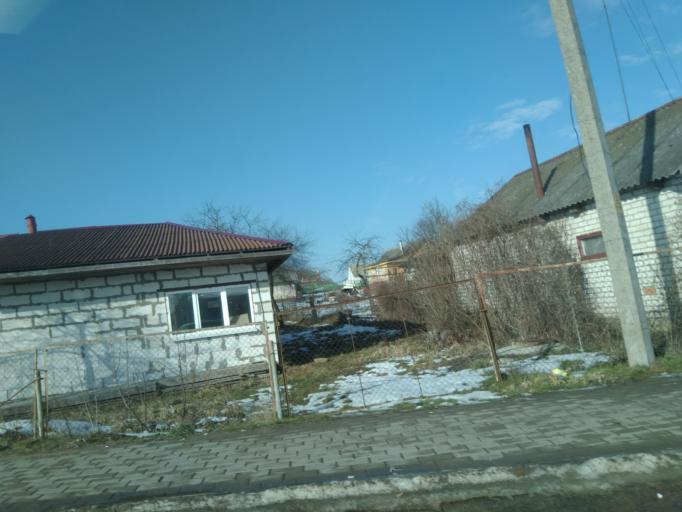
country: BY
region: Minsk
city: Nyasvizh
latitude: 53.2130
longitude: 26.6672
